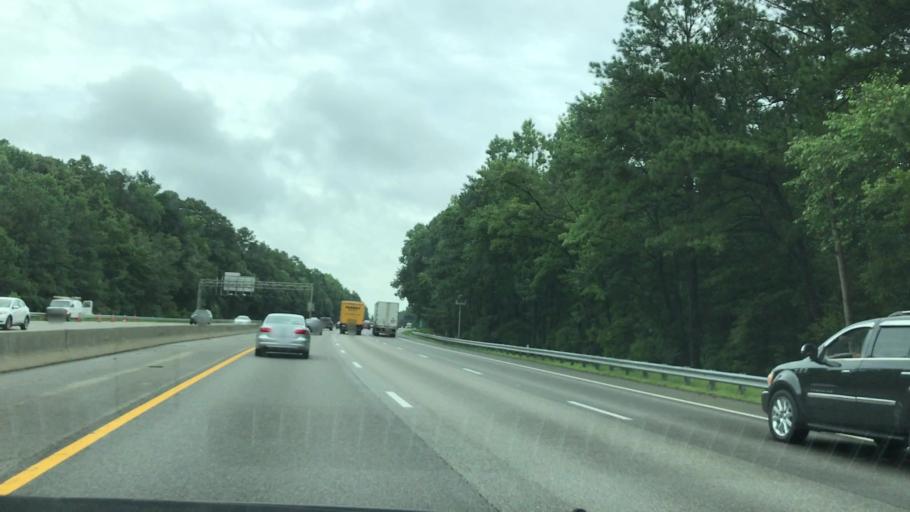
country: US
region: Virginia
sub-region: City of Colonial Heights
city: Colonial Heights
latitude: 37.3202
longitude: -77.4008
